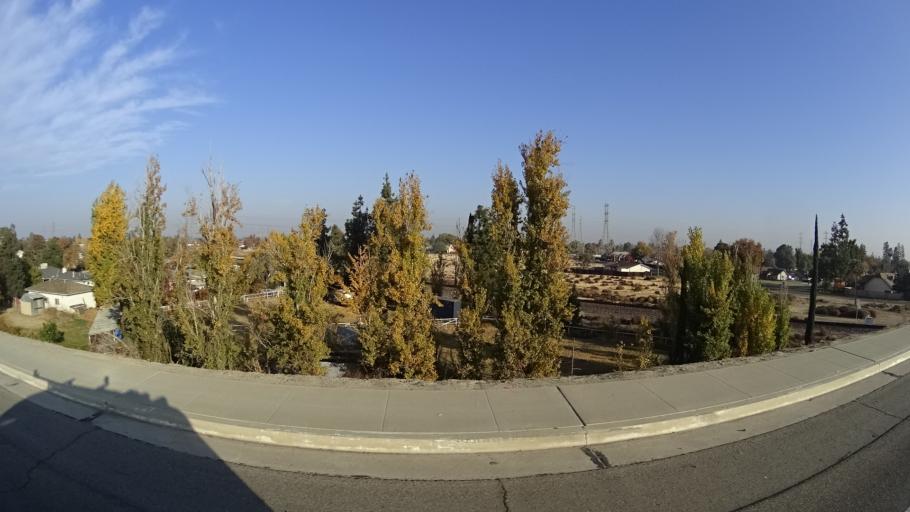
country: US
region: California
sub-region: Kern County
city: Rosedale
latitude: 35.3835
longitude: -119.1289
